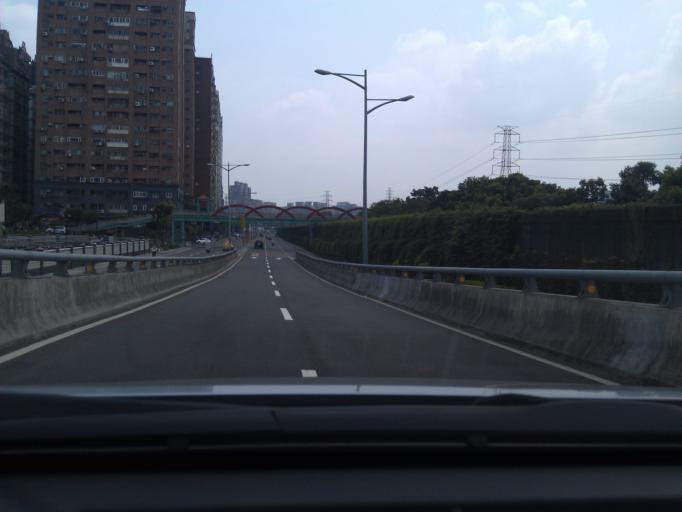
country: TW
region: Taipei
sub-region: Taipei
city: Banqiao
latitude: 25.0125
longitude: 121.5037
